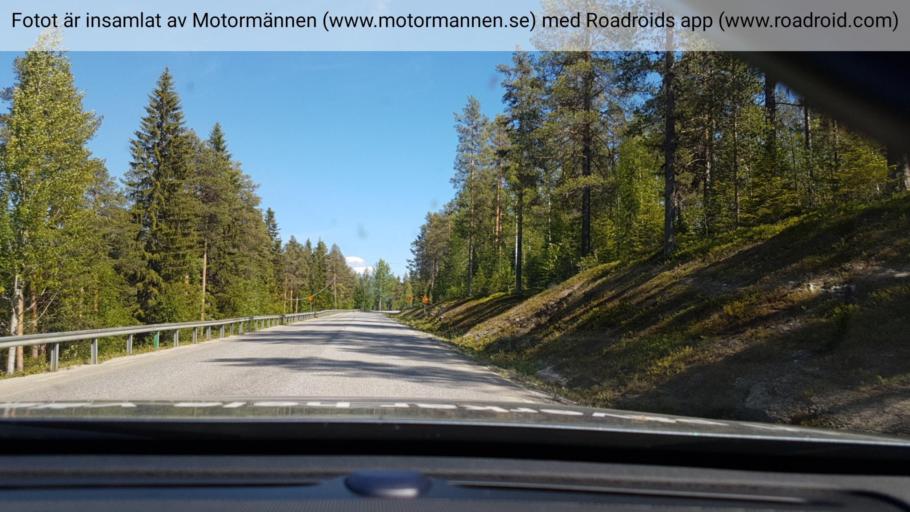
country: SE
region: Vaesterbotten
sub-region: Lycksele Kommun
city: Soderfors
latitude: 64.6153
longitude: 18.1799
